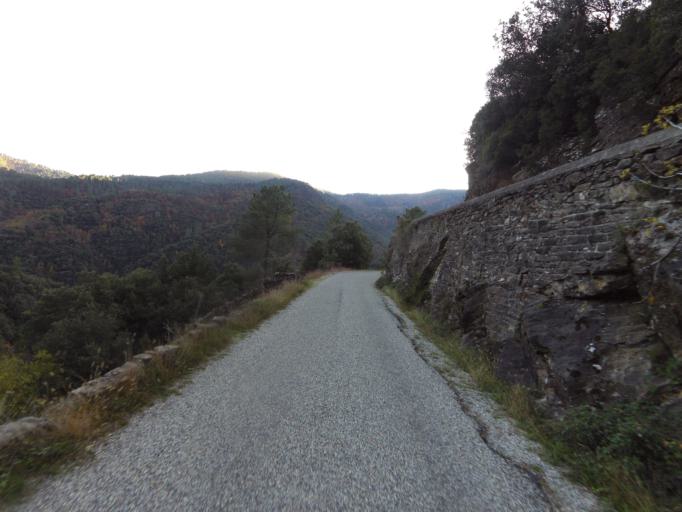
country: FR
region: Rhone-Alpes
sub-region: Departement de l'Ardeche
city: Lablachere
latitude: 44.5224
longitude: 4.1407
